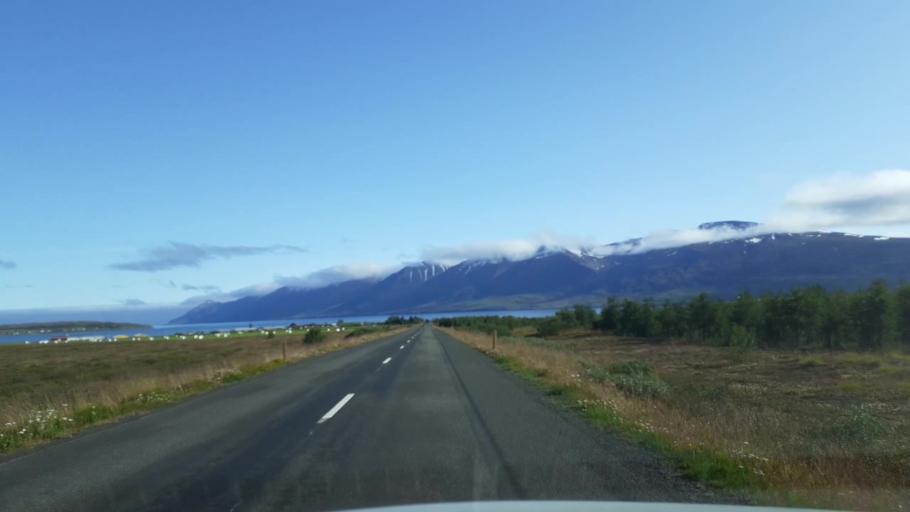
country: IS
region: Northeast
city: Dalvik
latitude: 65.9349
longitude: -18.3575
